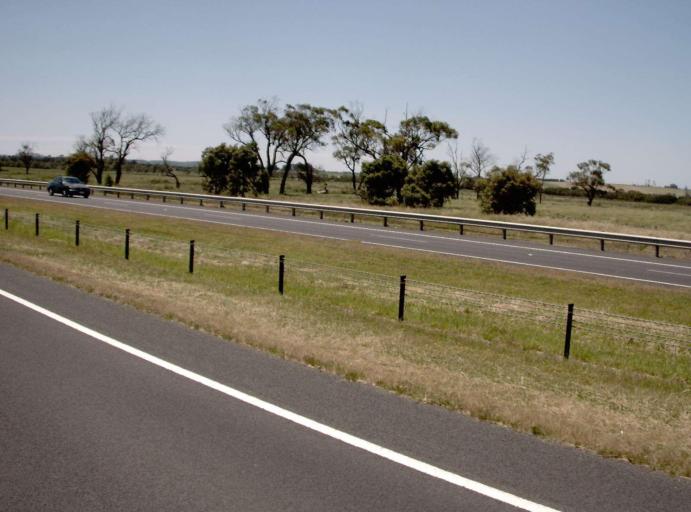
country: AU
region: Victoria
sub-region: Cardinia
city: Pakenham South
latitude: -38.0806
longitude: 145.5222
